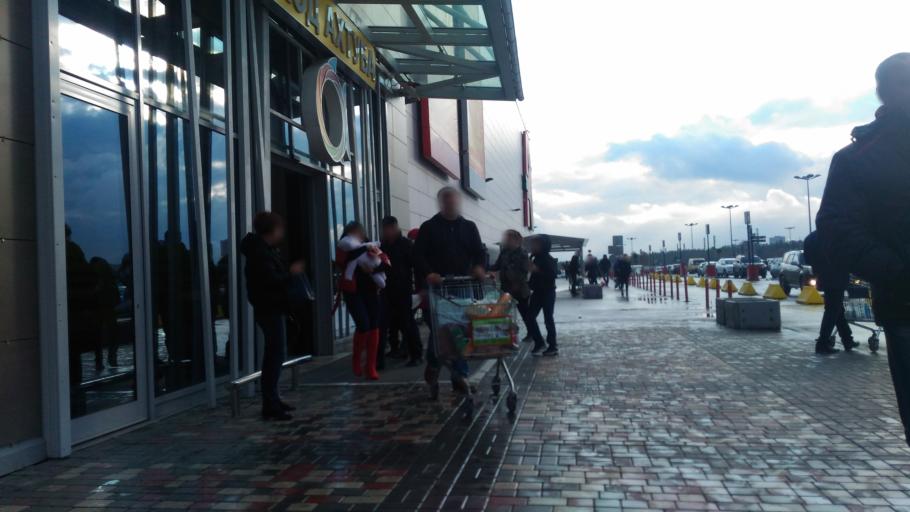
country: RU
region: Volgograd
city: Volgograd
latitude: 48.6360
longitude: 44.4349
